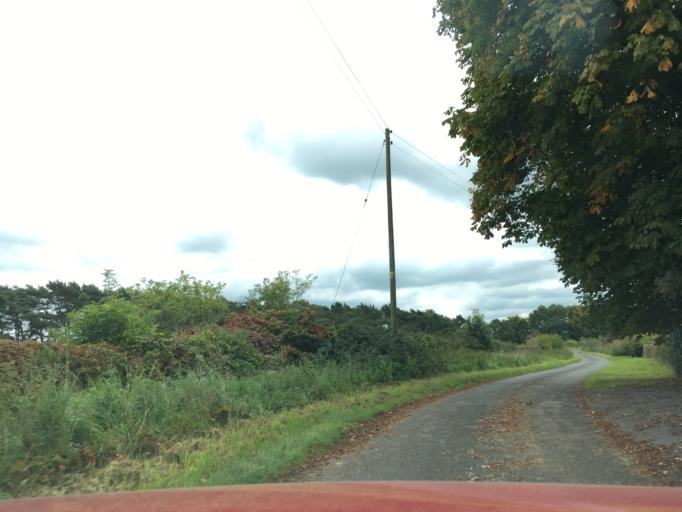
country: GB
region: England
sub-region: South Gloucestershire
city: Charfield
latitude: 51.6247
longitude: -2.4313
